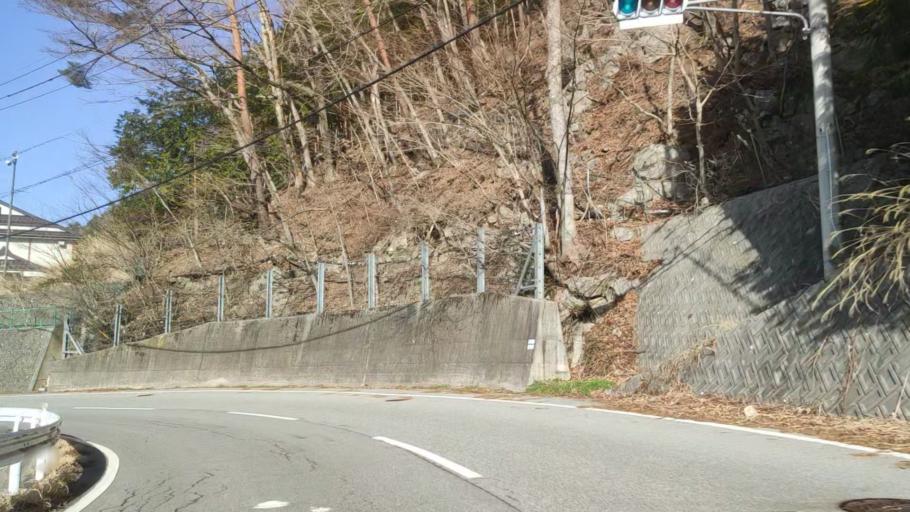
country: JP
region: Yamanashi
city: Fujikawaguchiko
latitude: 35.5554
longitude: 138.6721
